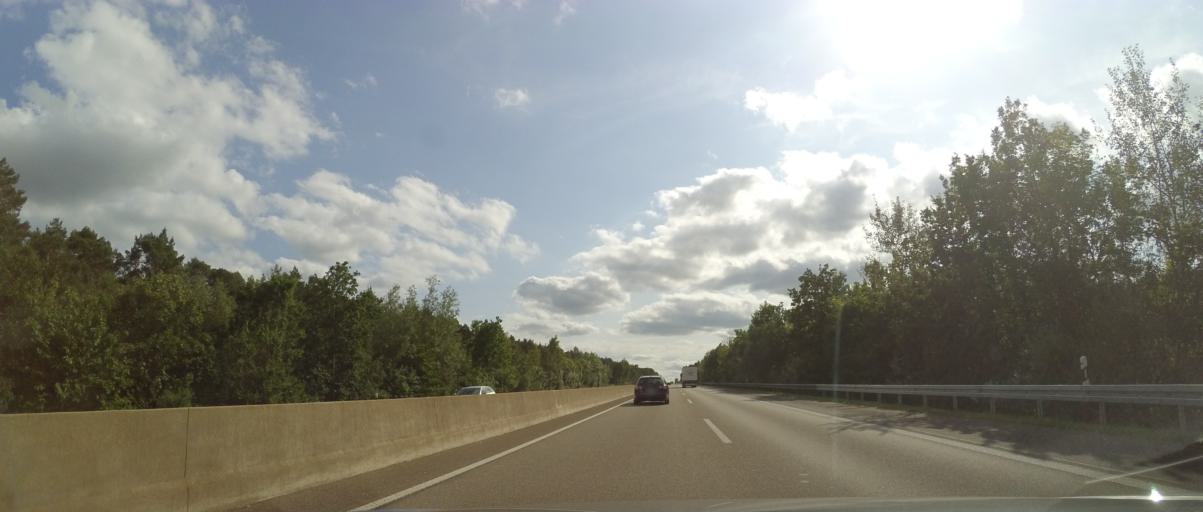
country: DE
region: North Rhine-Westphalia
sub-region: Regierungsbezirk Koln
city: Mechernich
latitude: 50.5976
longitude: 6.7027
